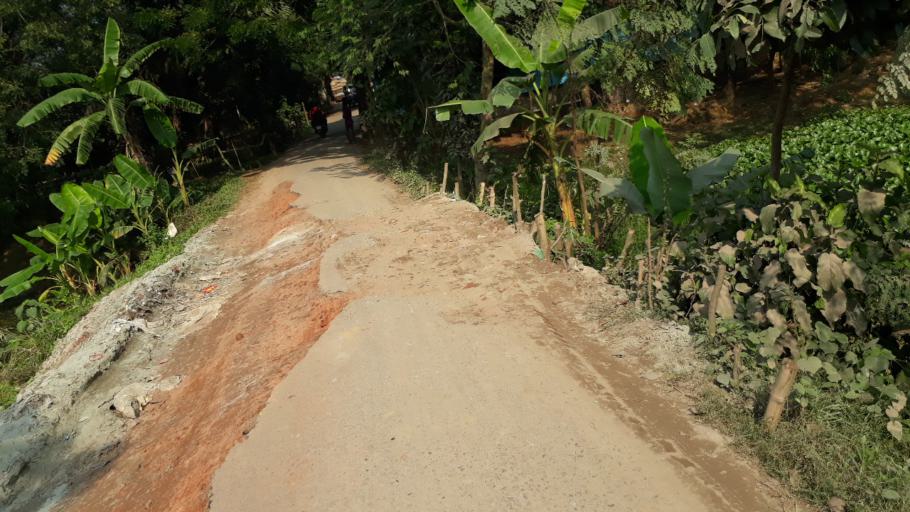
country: BD
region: Dhaka
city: Tungi
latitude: 23.8750
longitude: 90.2593
